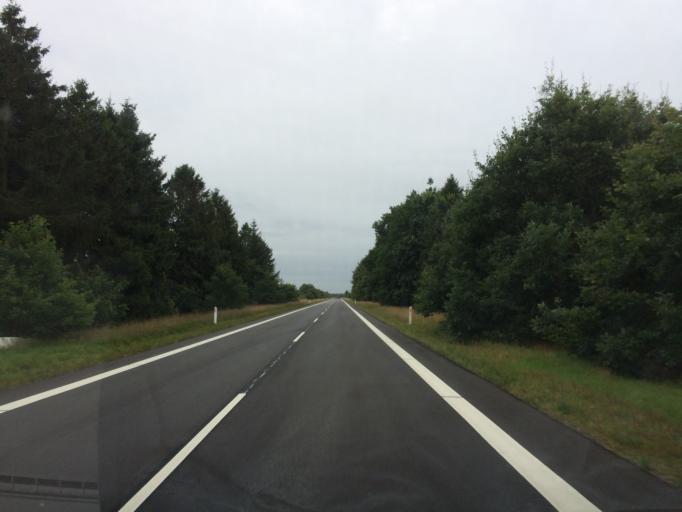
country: DK
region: Central Jutland
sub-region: Herning Kommune
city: Lind
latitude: 56.0464
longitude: 8.9971
